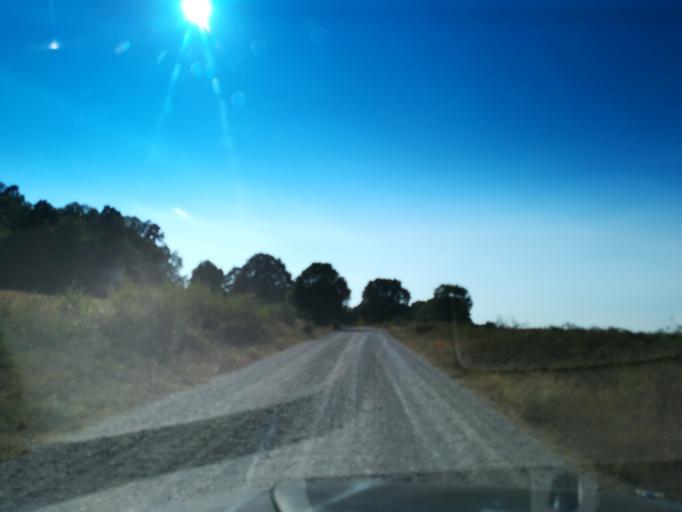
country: BG
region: Khaskovo
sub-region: Obshtina Mineralni Bani
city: Mineralni Bani
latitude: 41.9715
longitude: 25.3369
